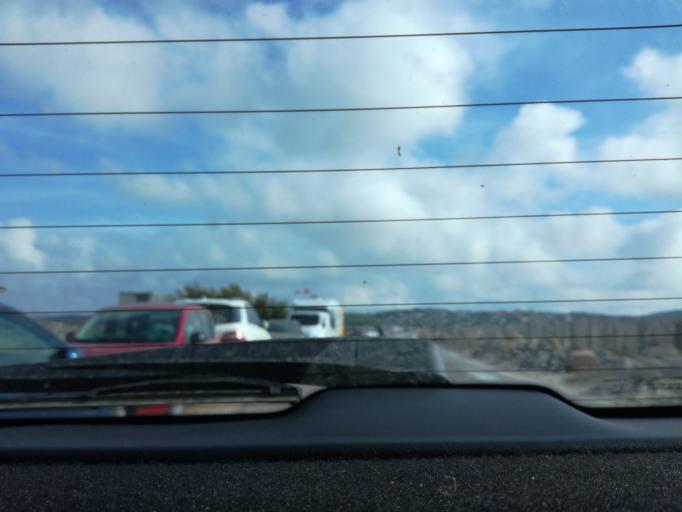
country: FR
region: Provence-Alpes-Cote d'Azur
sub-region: Departement du Var
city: Hyeres
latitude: 43.0568
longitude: 6.1336
